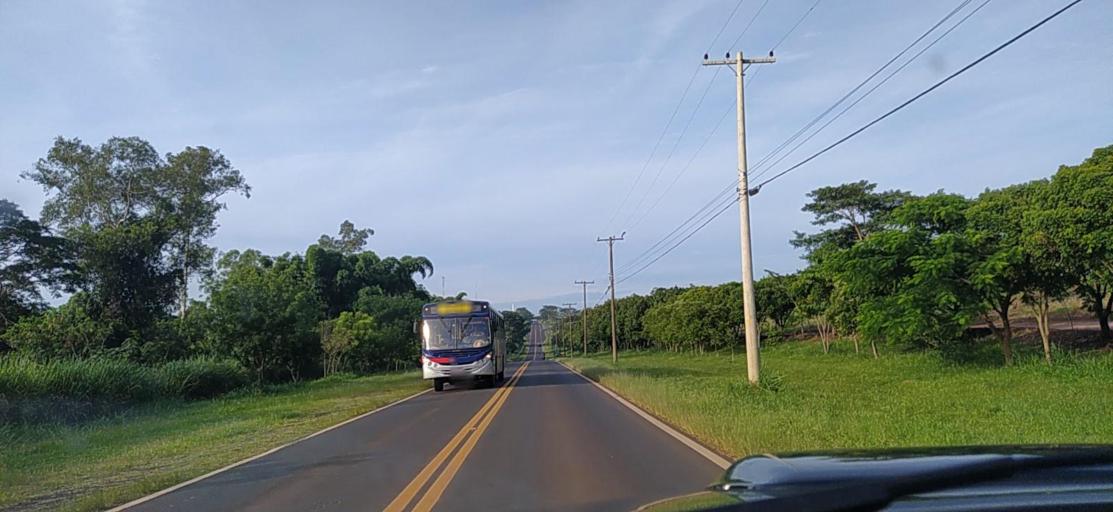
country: BR
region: Sao Paulo
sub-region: Pindorama
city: Pindorama
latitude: -21.2021
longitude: -48.9261
